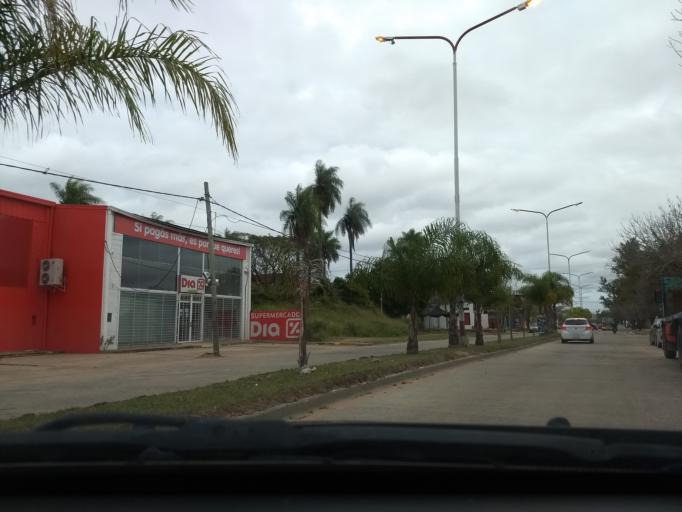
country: AR
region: Corrientes
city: Corrientes
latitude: -27.4770
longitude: -58.7866
